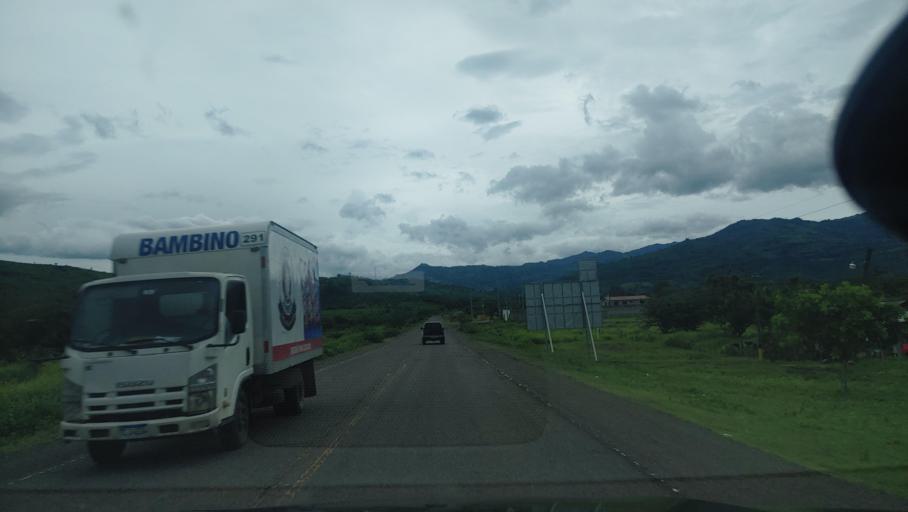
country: HN
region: Choluteca
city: Santa Ana de Yusguare
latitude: 13.3534
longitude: -87.1043
